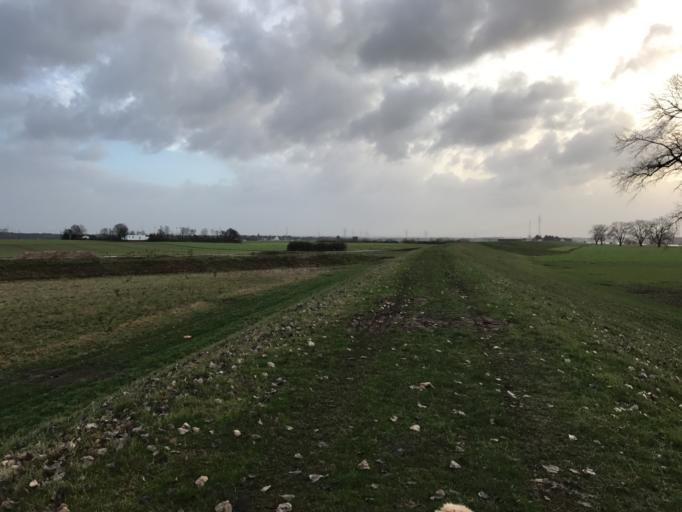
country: DE
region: North Rhine-Westphalia
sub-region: Regierungsbezirk Dusseldorf
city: Meerbusch
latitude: 51.3485
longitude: 6.6791
